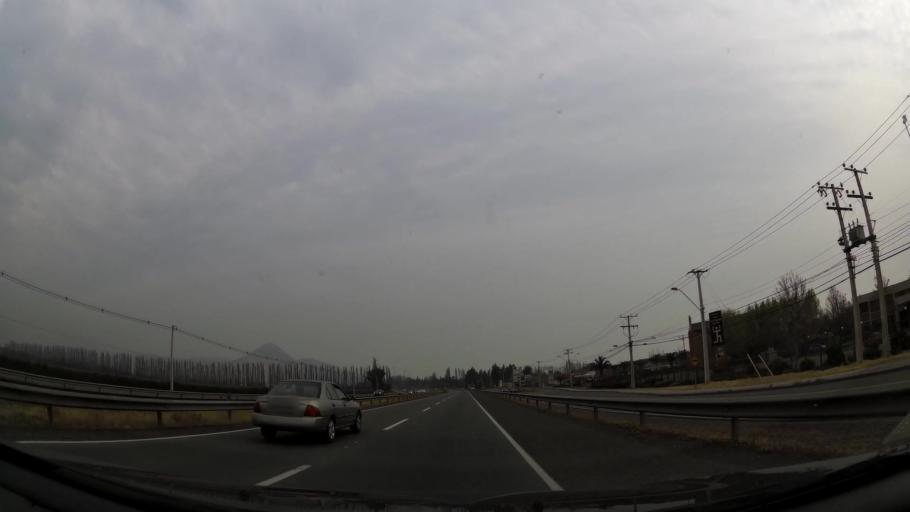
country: CL
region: Santiago Metropolitan
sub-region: Provincia de Chacabuco
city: Chicureo Abajo
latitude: -33.2752
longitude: -70.7021
